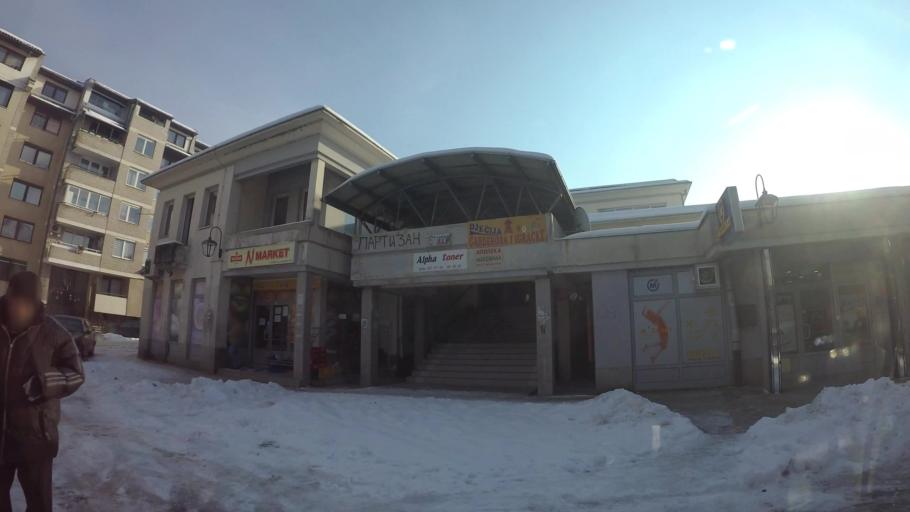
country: BA
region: Federation of Bosnia and Herzegovina
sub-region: Kanton Sarajevo
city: Sarajevo
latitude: 43.8274
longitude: 18.3579
